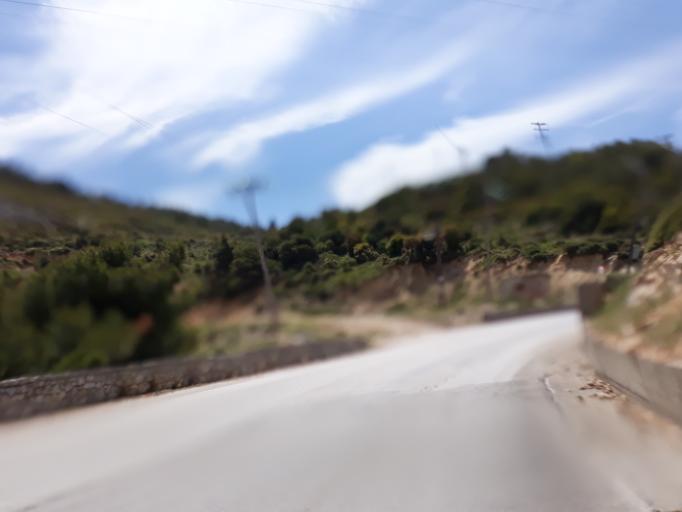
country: GR
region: Attica
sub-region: Nomarchia Dytikis Attikis
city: Magoula
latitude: 38.1703
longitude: 23.5478
